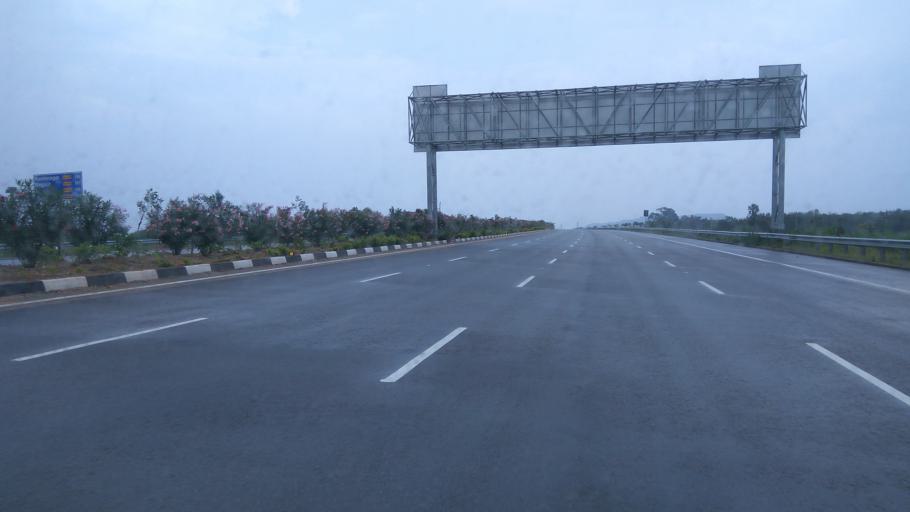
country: IN
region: Telangana
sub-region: Rangareddi
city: Ghatkesar
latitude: 17.4610
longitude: 78.6703
